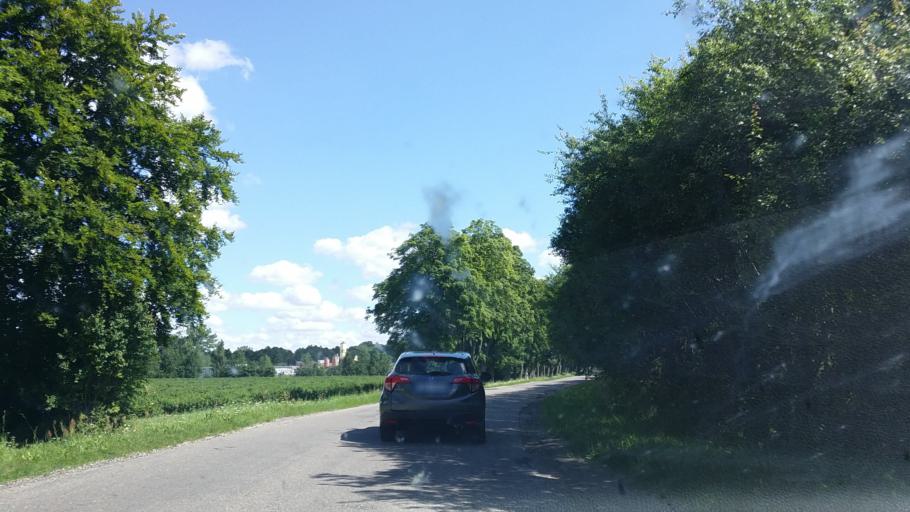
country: PL
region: West Pomeranian Voivodeship
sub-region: Powiat swidwinski
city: Swidwin
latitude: 53.7605
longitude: 15.7659
